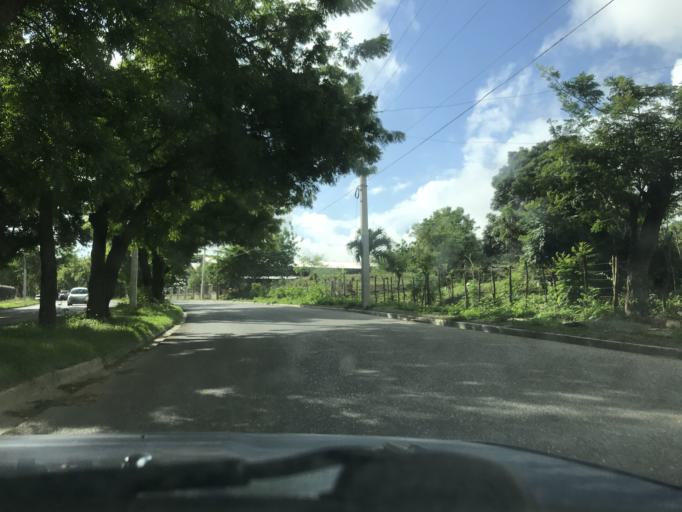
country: DO
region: Santiago
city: Santiago de los Caballeros
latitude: 19.4137
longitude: -70.7283
